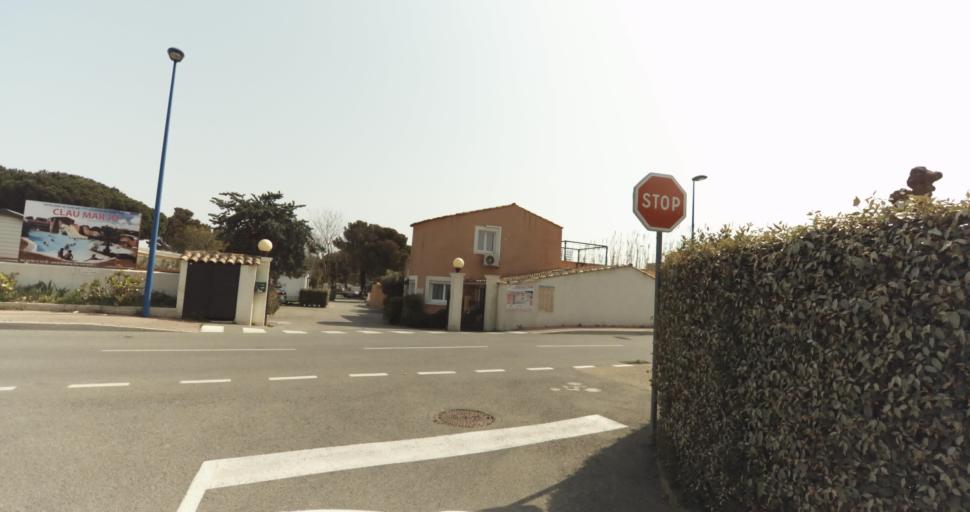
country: FR
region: Provence-Alpes-Cote d'Azur
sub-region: Departement du Var
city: Bormes-les-Mimosas
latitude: 43.1347
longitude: 6.3464
